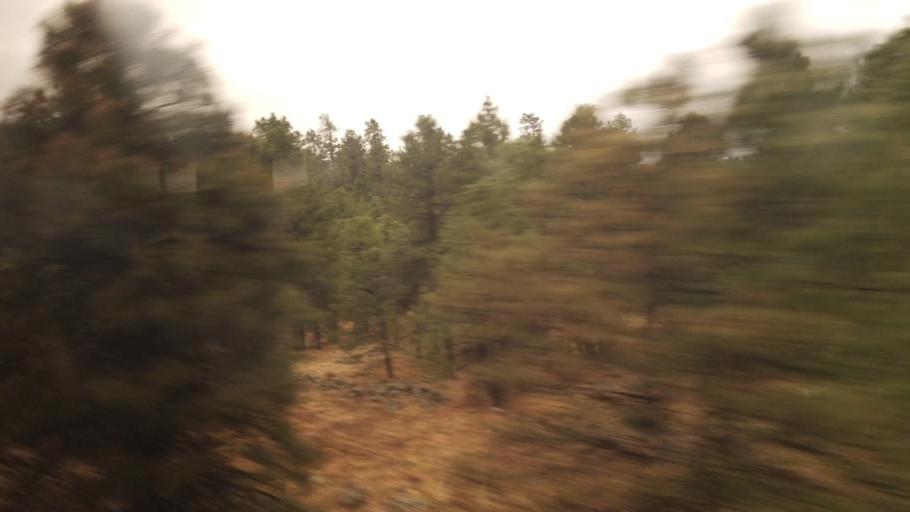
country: US
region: Arizona
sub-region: Coconino County
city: Parks
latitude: 35.2437
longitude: -111.8806
